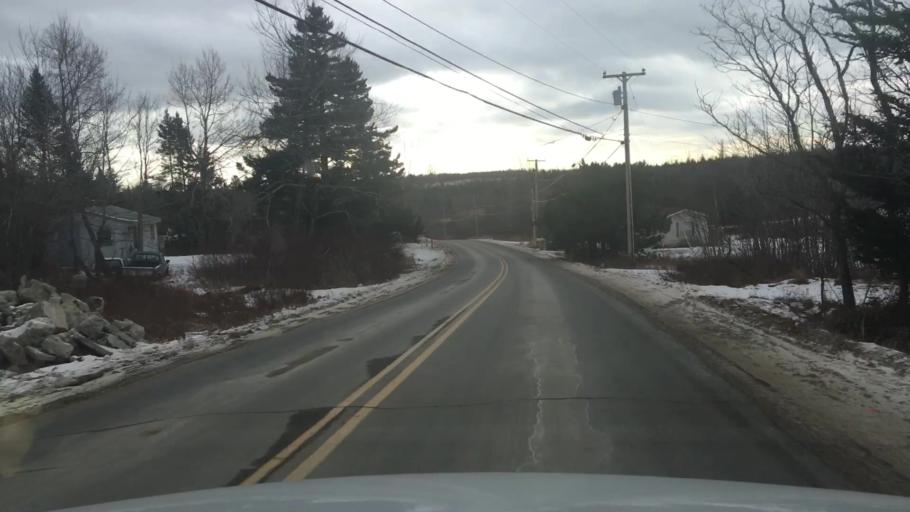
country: US
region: Maine
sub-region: Washington County
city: Machias
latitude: 44.6848
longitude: -67.4666
